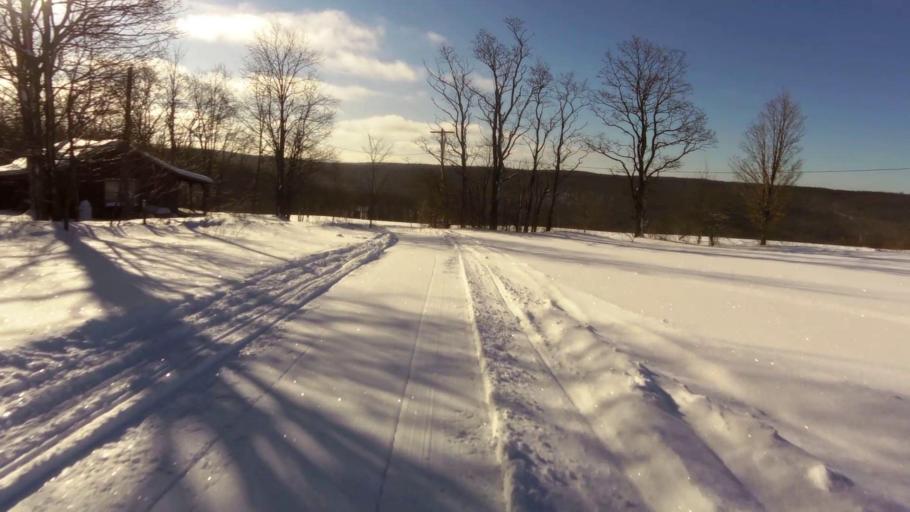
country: US
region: New York
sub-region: Chautauqua County
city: Falconer
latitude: 42.2612
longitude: -79.1810
